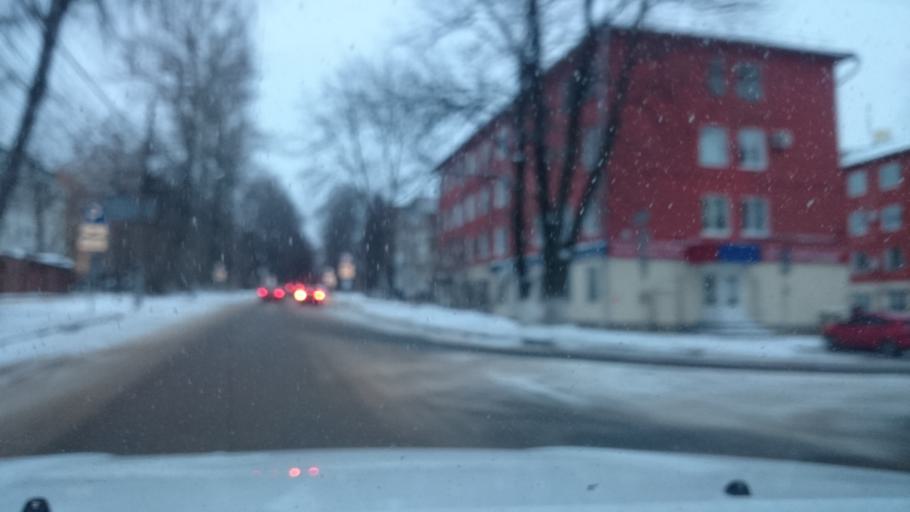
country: RU
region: Tula
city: Tula
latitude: 54.1808
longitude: 37.6067
